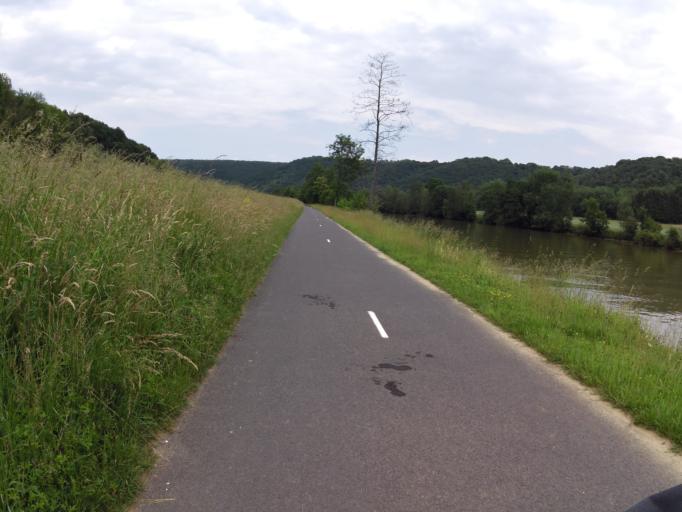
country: FR
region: Champagne-Ardenne
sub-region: Departement des Ardennes
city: Aiglemont
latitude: 49.7868
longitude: 4.7552
